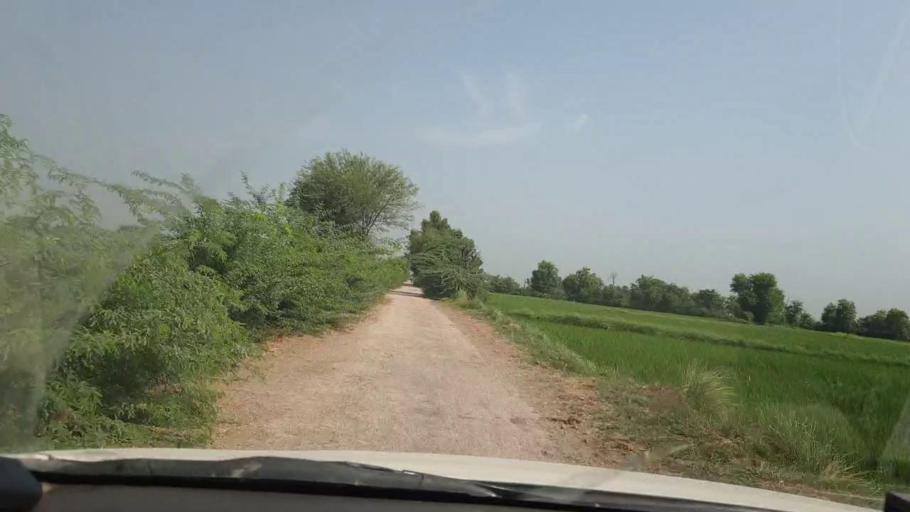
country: PK
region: Sindh
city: Chak
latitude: 27.8317
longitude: 68.7995
